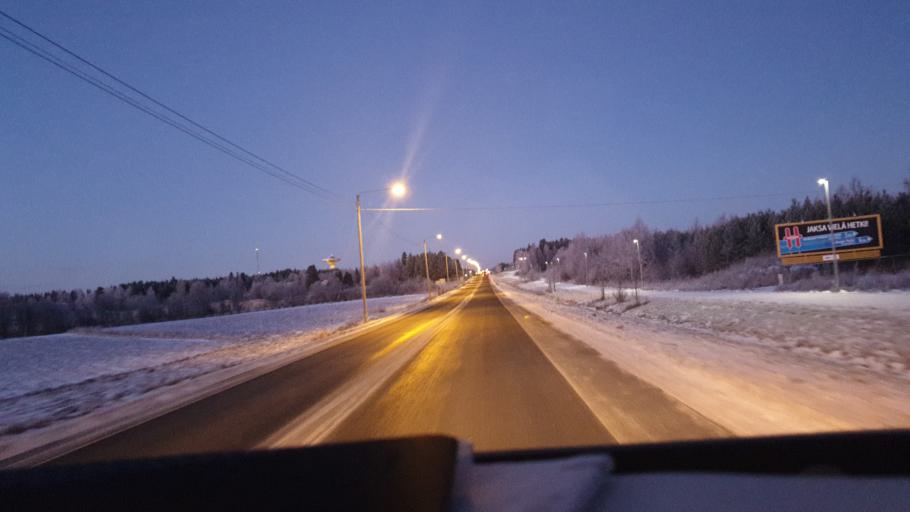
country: FI
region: Northern Ostrobothnia
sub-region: Raahe
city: Raahe
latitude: 64.6875
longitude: 24.5884
